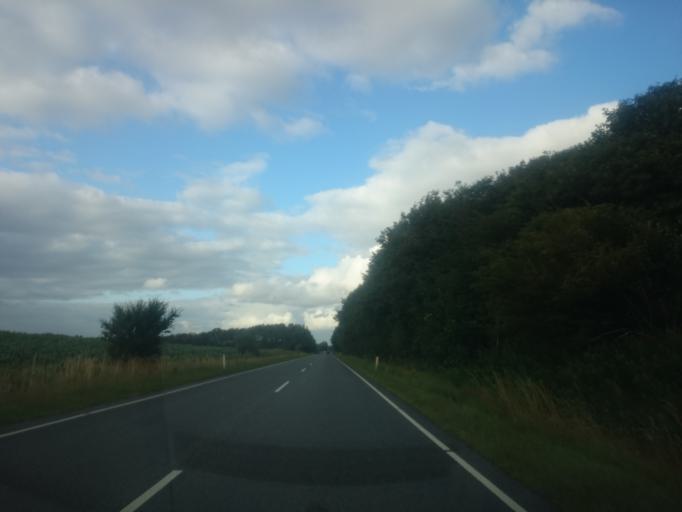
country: DK
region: South Denmark
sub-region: Varde Kommune
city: Olgod
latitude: 55.6582
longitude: 8.6913
